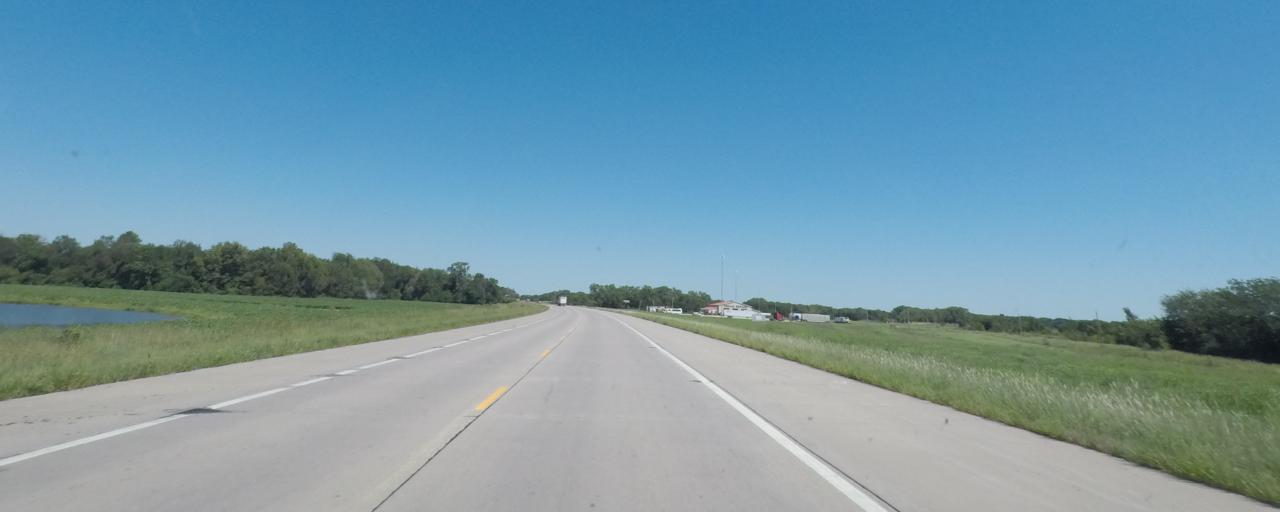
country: US
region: Kansas
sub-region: Lyon County
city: Emporia
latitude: 38.4066
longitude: -96.3084
